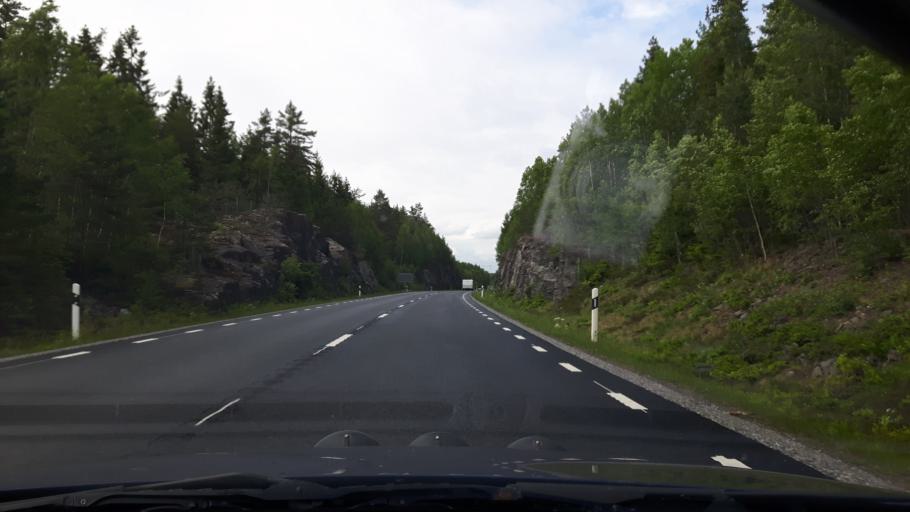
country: SE
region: Soedermanland
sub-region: Flens Kommun
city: Flen
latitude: 59.0648
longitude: 16.6202
